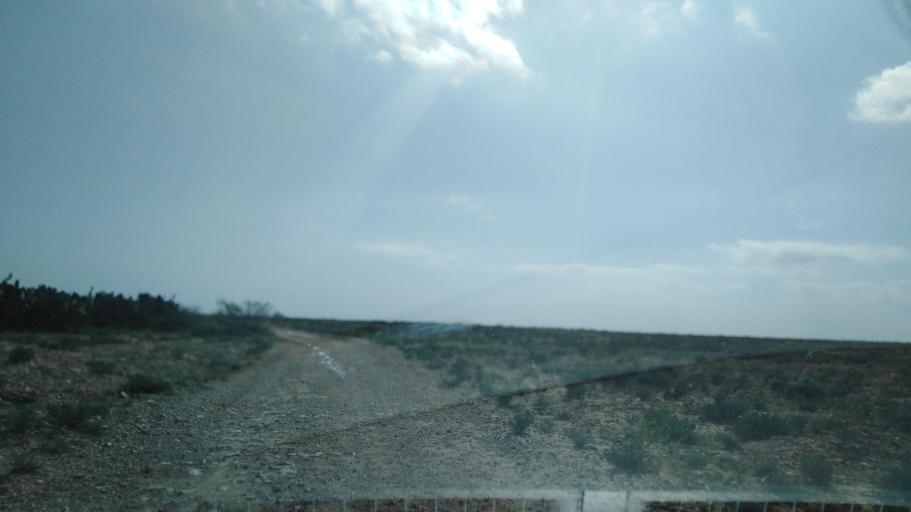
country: TN
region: Safaqis
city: Bi'r `Ali Bin Khalifah
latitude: 34.7986
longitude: 10.3756
